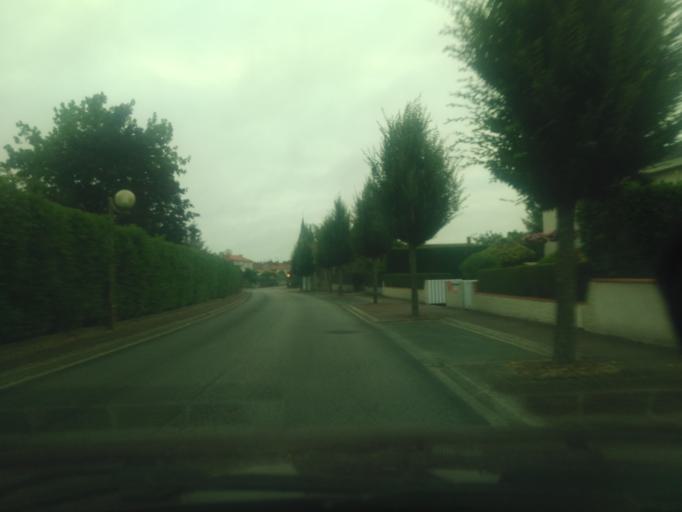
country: FR
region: Pays de la Loire
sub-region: Departement de la Vendee
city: La Ferriere
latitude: 46.7669
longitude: -1.3021
